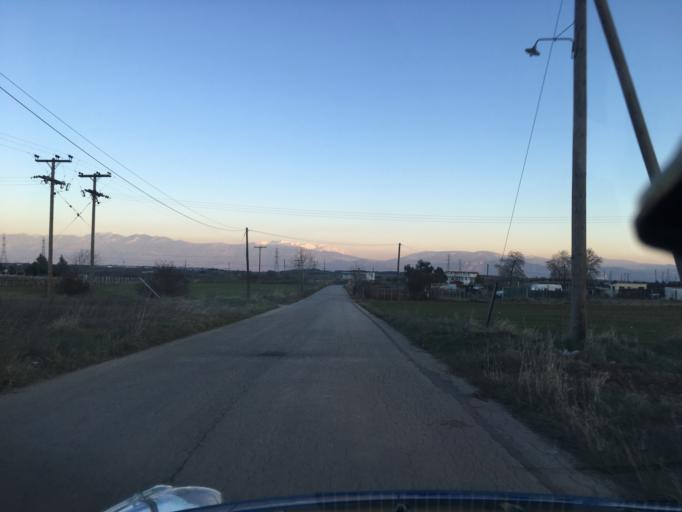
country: GR
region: West Macedonia
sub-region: Nomos Kozanis
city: Kozani
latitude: 40.2576
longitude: 21.7554
